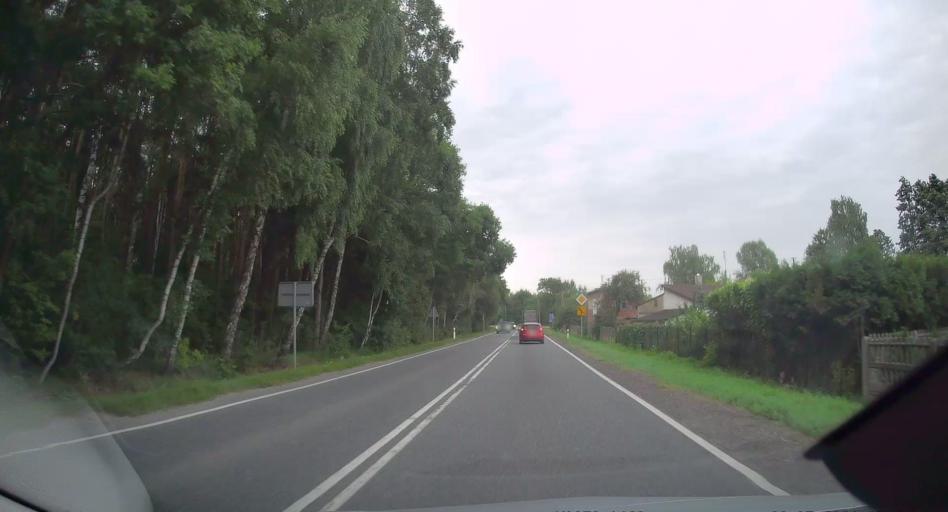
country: PL
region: Lodz Voivodeship
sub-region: Powiat radomszczanski
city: Kamiensk
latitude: 51.1874
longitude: 19.4962
